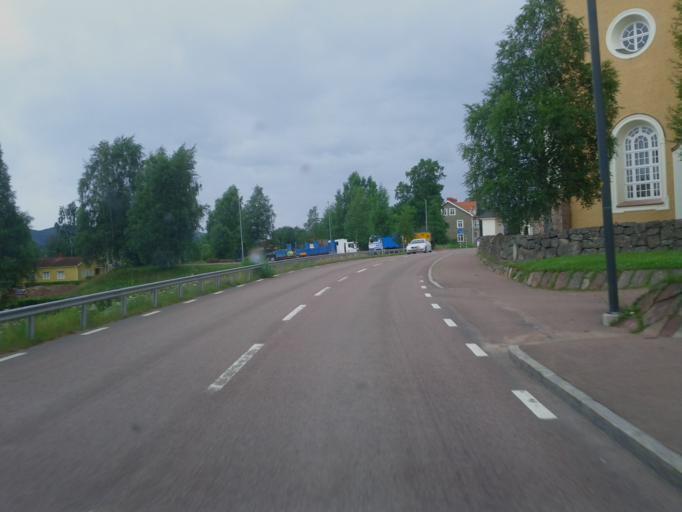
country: SE
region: Dalarna
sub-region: Alvdalens Kommun
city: AElvdalen
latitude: 61.2253
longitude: 14.0426
